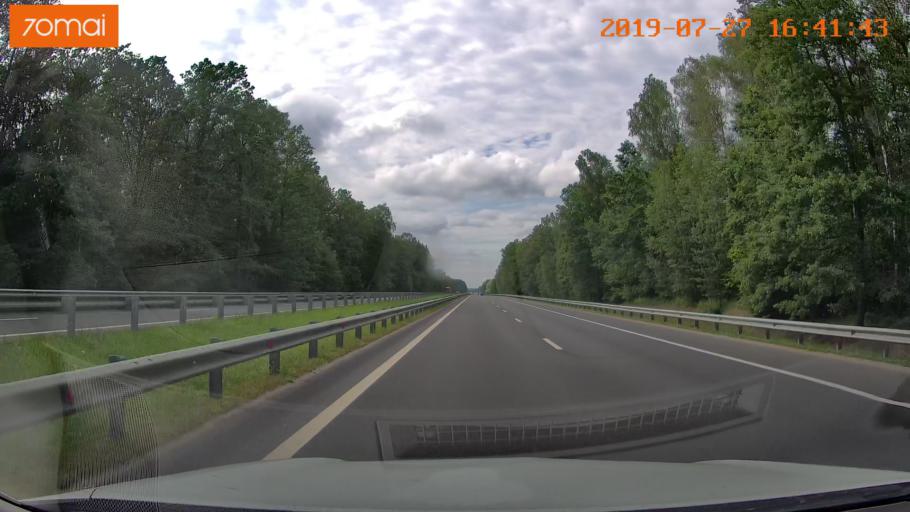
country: RU
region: Kaliningrad
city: Gvardeysk
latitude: 54.6581
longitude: 21.1411
